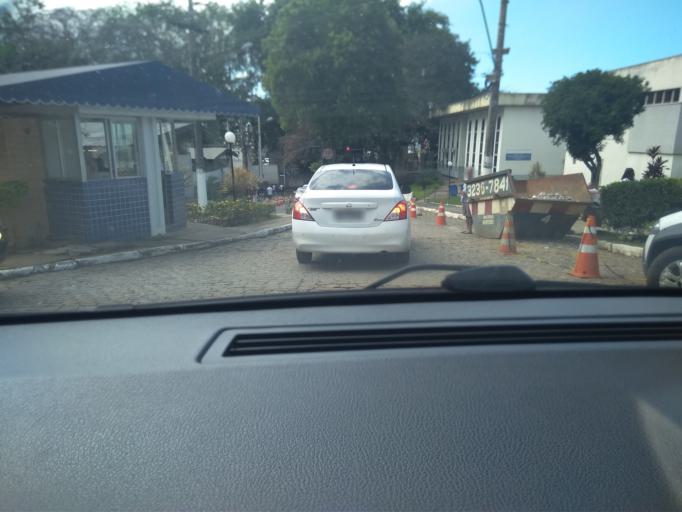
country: BR
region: Espirito Santo
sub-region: Vitoria
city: Vitoria
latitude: -20.2993
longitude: -40.3174
